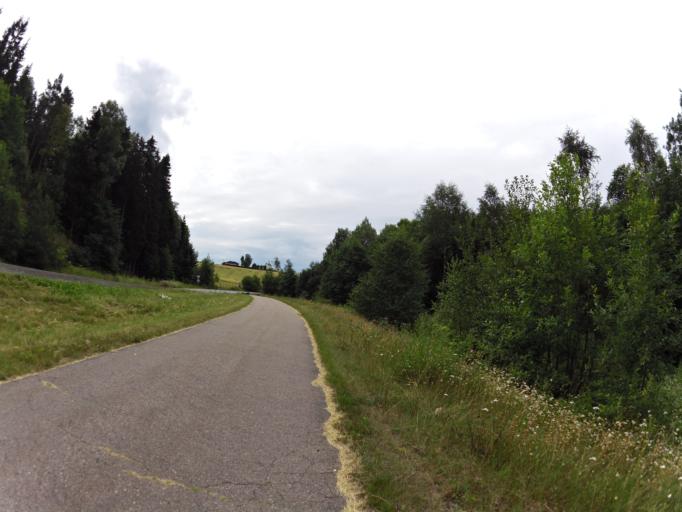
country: NO
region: Akershus
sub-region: As
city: As
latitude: 59.7062
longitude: 10.7395
